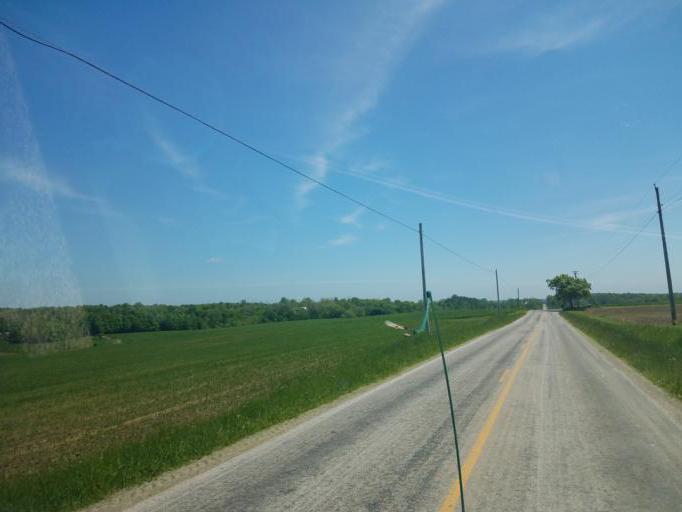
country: US
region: Ohio
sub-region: Wayne County
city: West Salem
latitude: 40.9448
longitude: -82.2003
